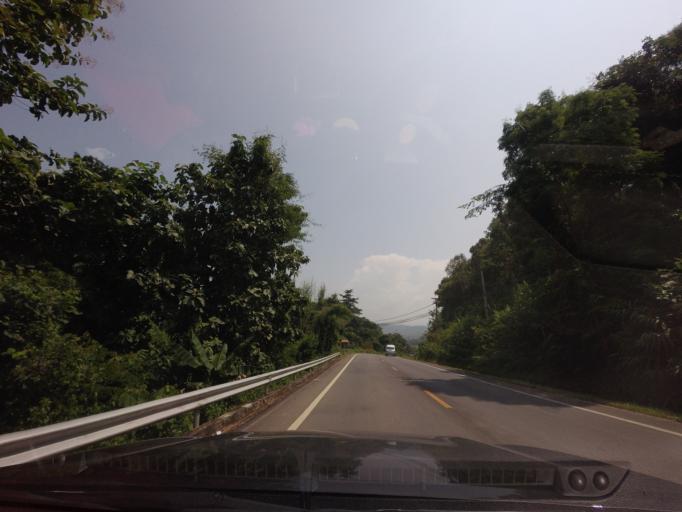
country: TH
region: Nan
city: Santi Suk
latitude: 18.9241
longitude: 100.9195
